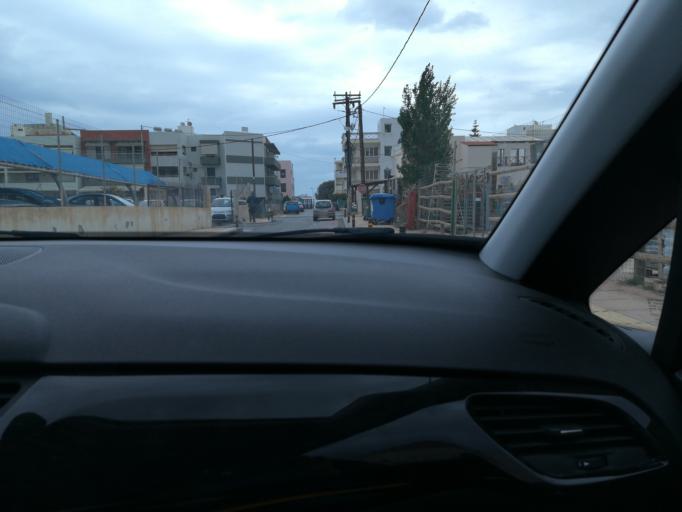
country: GR
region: Crete
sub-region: Nomos Lasithiou
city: Siteia
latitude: 35.2051
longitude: 26.1070
